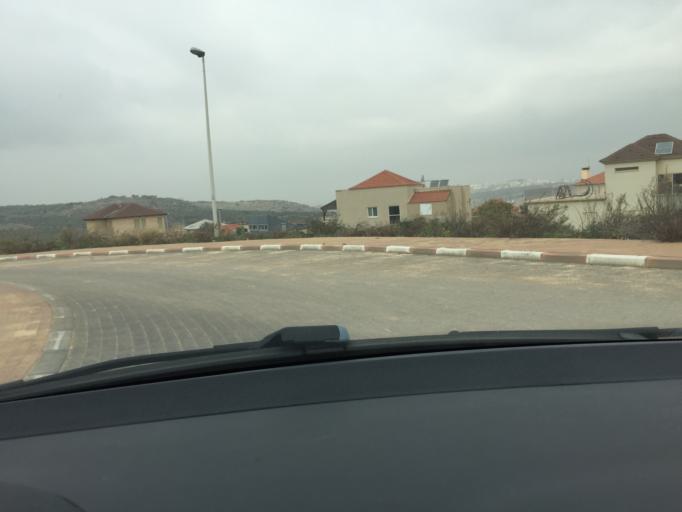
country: PS
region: West Bank
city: Al Lubban al Gharbi
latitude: 32.0442
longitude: 35.0462
